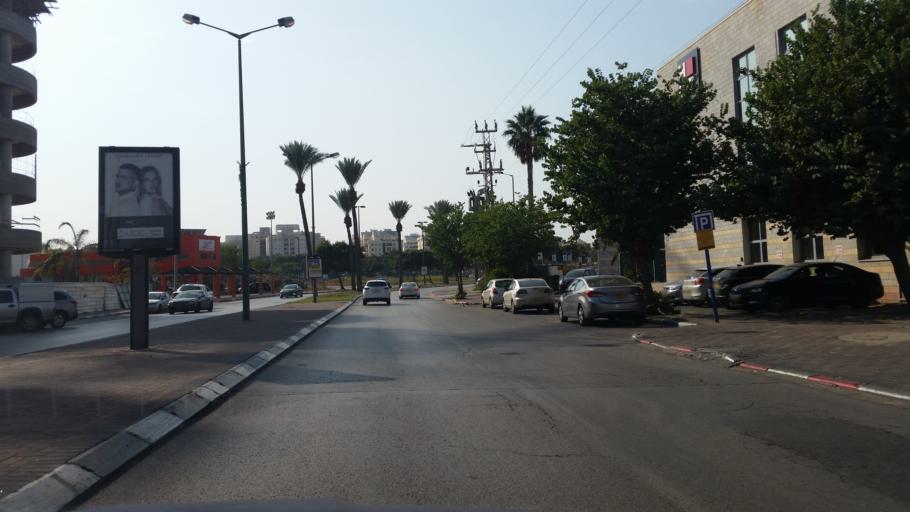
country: IL
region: Central District
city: Bet Yizhaq
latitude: 32.3144
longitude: 34.8735
